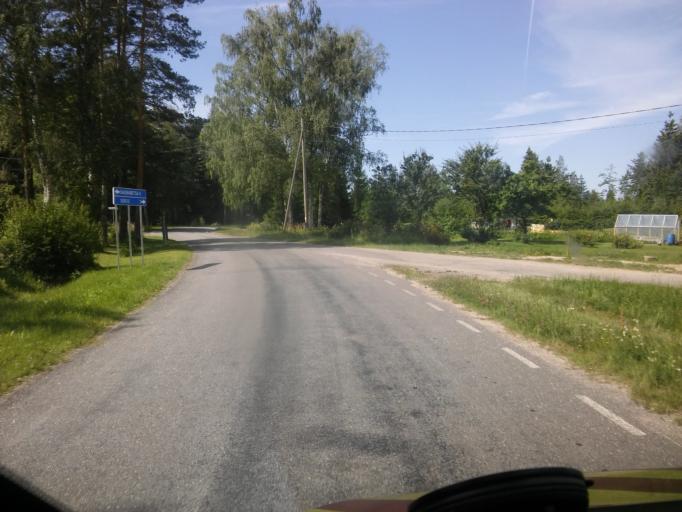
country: EE
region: Paernumaa
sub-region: Sindi linn
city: Sindi
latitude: 58.2482
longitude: 24.7448
